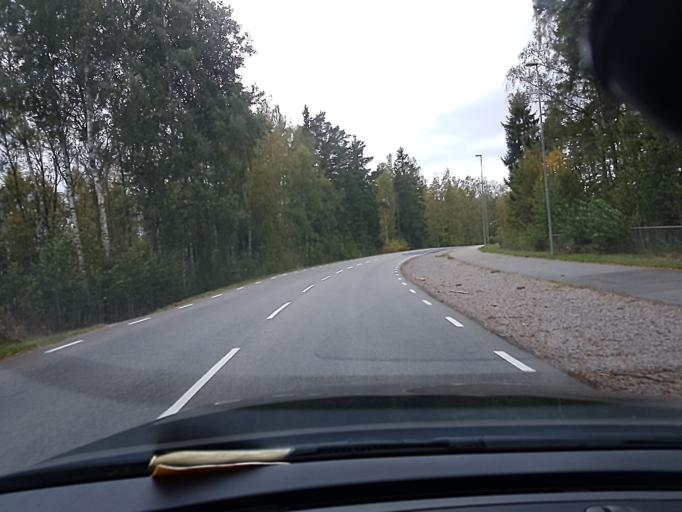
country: SE
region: Kronoberg
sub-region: Vaxjo Kommun
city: Vaexjoe
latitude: 56.9127
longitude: 14.8150
